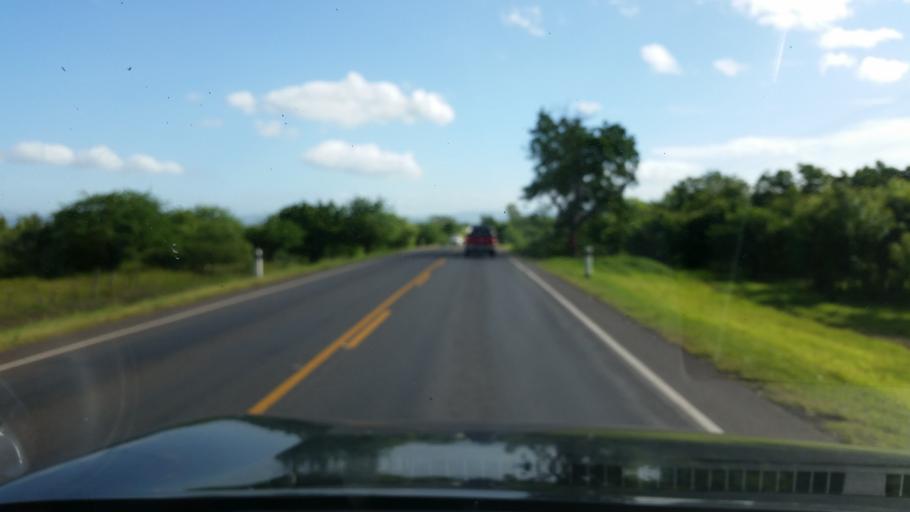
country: NI
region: Managua
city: Tipitapa
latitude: 12.3260
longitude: -86.0526
